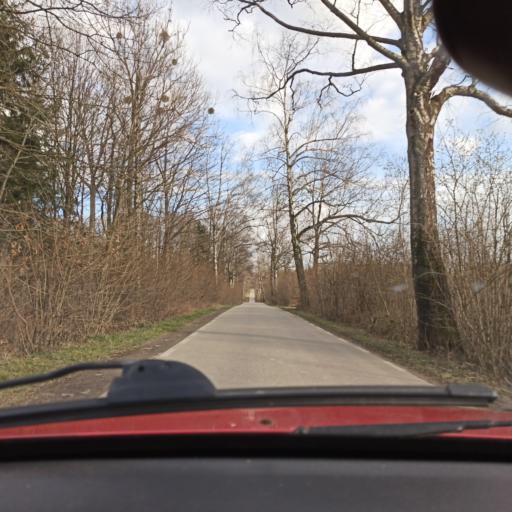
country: PL
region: Warmian-Masurian Voivodeship
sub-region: Powiat elblaski
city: Tolkmicko
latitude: 54.2621
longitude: 19.4941
